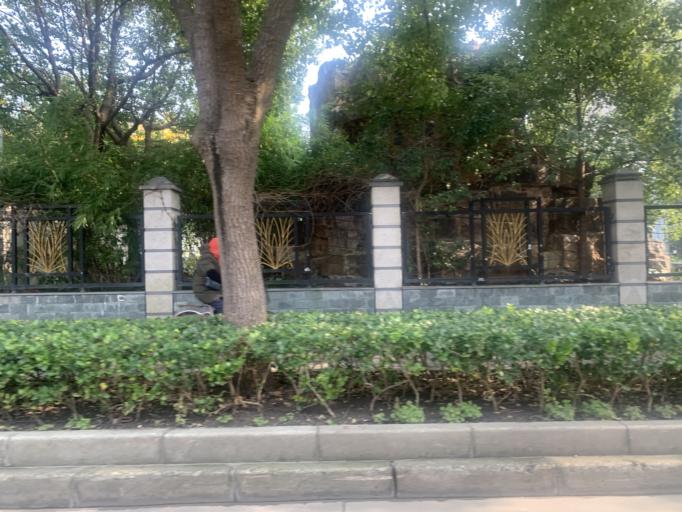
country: CN
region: Shanghai Shi
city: Huamu
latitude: 31.1832
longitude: 121.5155
